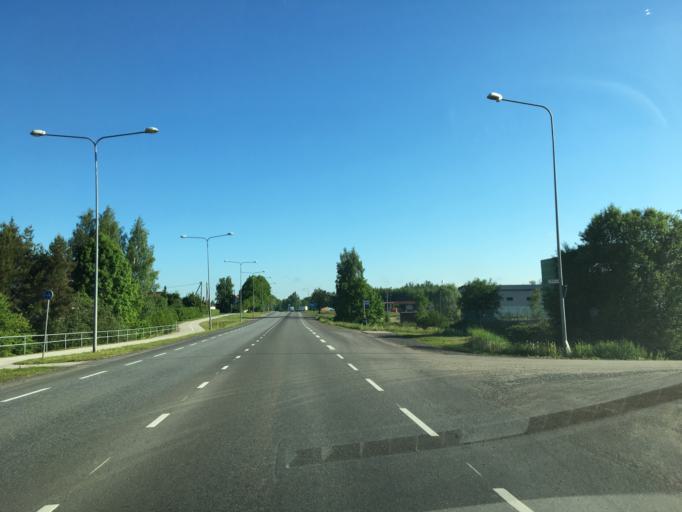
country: EE
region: Tartu
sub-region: Tartu linn
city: Tartu
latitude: 58.4040
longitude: 26.7084
